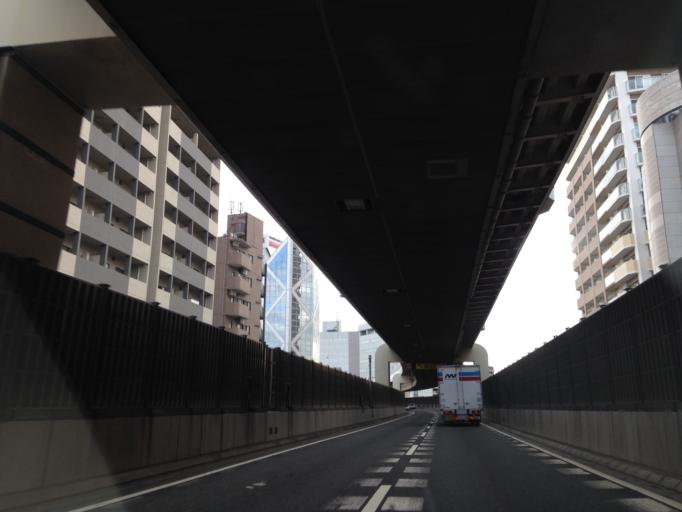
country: JP
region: Saitama
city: Kawaguchi
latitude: 35.7461
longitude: 139.7257
